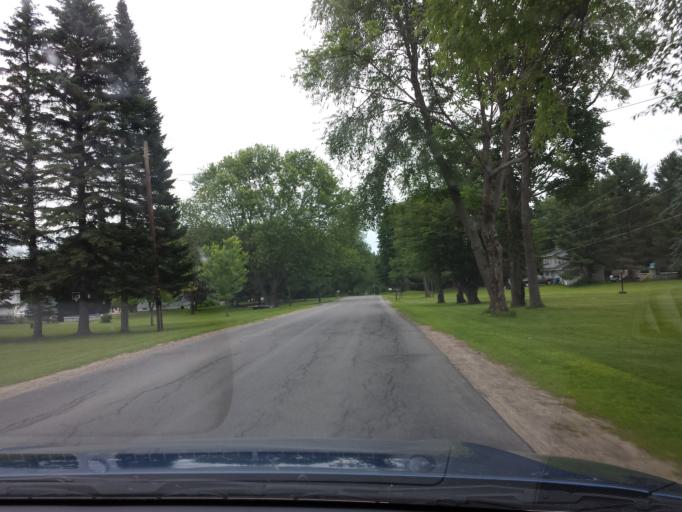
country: US
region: New York
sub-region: St. Lawrence County
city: Potsdam
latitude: 44.6953
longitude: -74.9688
